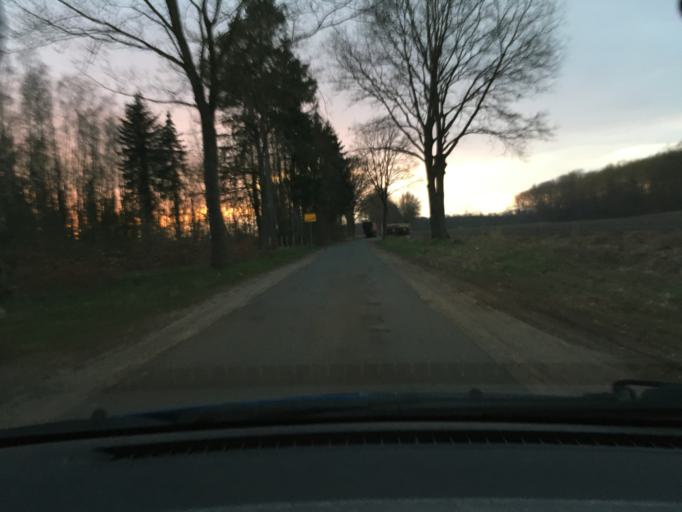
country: DE
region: Lower Saxony
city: Neetze
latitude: 53.3011
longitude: 10.6697
